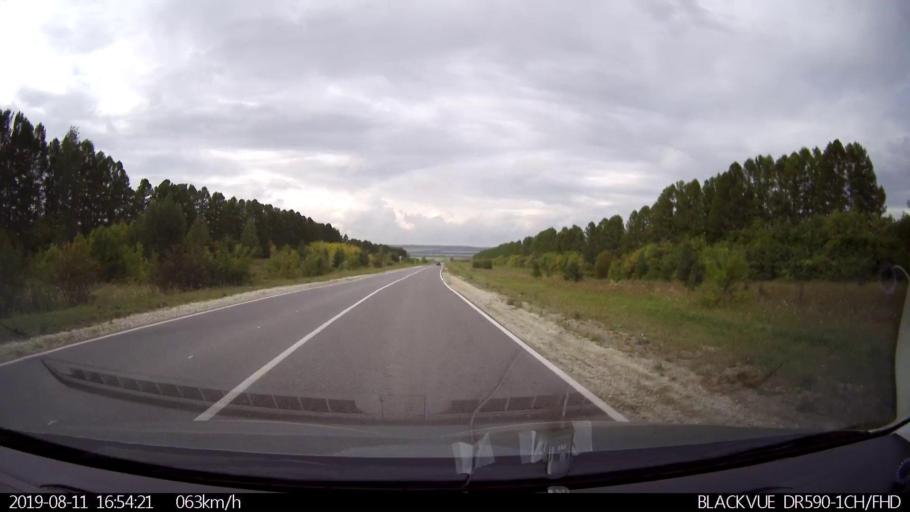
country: RU
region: Ulyanovsk
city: Mayna
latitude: 54.2719
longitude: 47.6665
